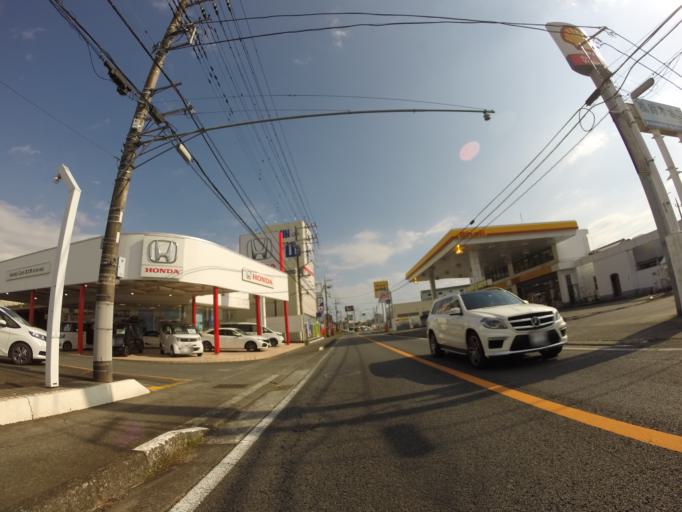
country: JP
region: Shizuoka
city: Fujinomiya
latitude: 35.2148
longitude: 138.6303
